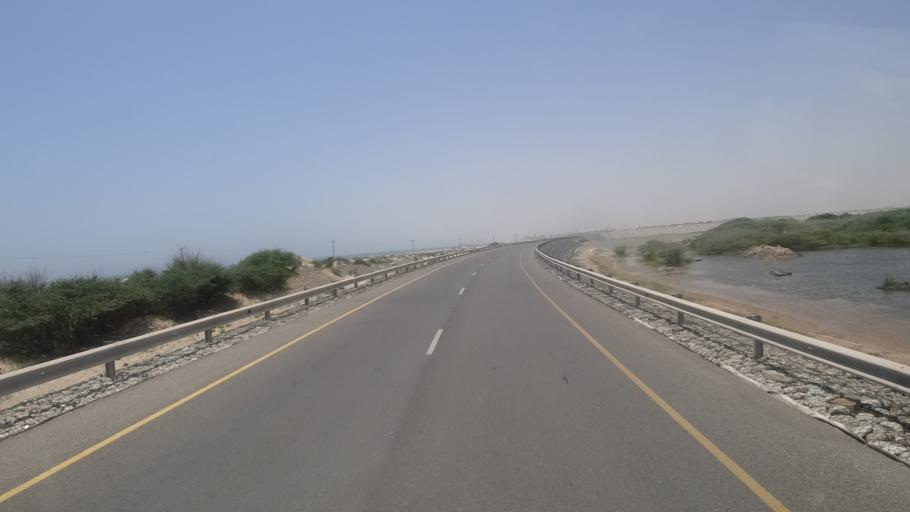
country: OM
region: Ash Sharqiyah
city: Sur
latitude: 22.0955
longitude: 59.6967
